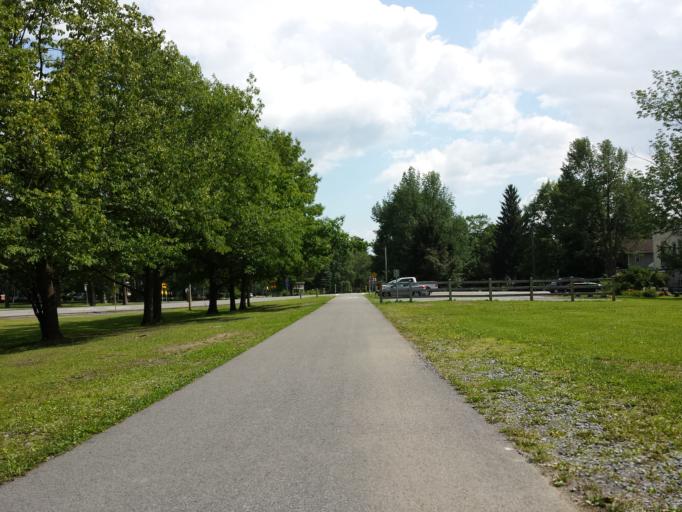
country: US
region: New York
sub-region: Saratoga County
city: Country Knolls
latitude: 42.9378
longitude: -73.7969
